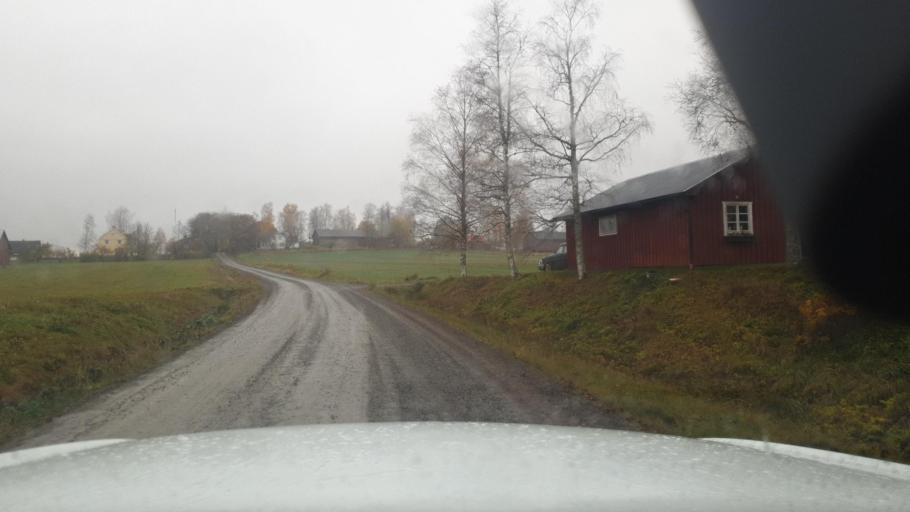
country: SE
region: Vaermland
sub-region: Sunne Kommun
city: Sunne
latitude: 59.8115
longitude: 13.0623
